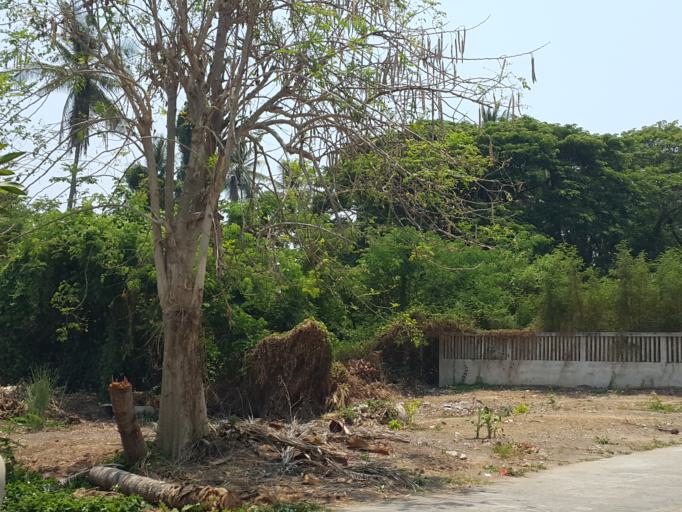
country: TH
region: Phitsanulok
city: Phitsanulok
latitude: 16.8185
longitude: 100.2492
